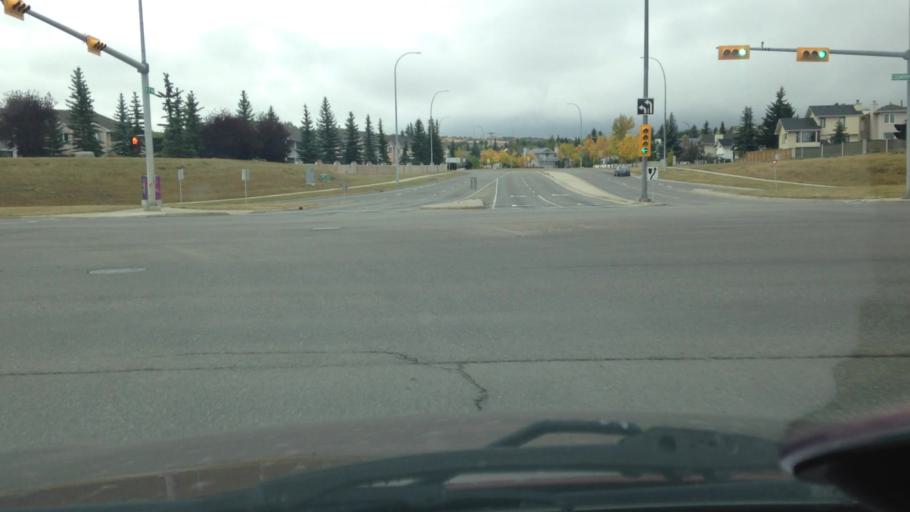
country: CA
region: Alberta
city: Calgary
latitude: 51.1435
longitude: -114.1079
